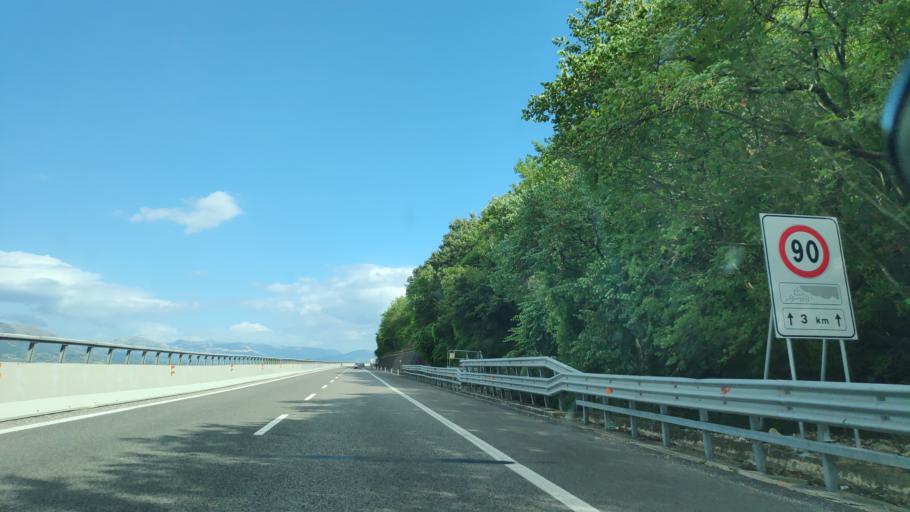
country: IT
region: Campania
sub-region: Provincia di Salerno
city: Sicignano degli Alburni
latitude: 40.5973
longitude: 15.3180
